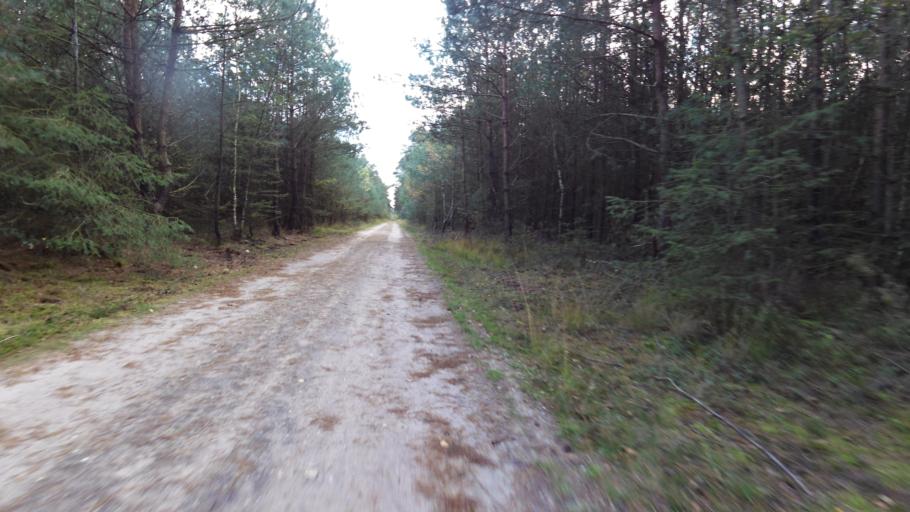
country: NL
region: Gelderland
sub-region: Gemeente Nunspeet
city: Nunspeet
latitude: 52.3180
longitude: 5.8382
